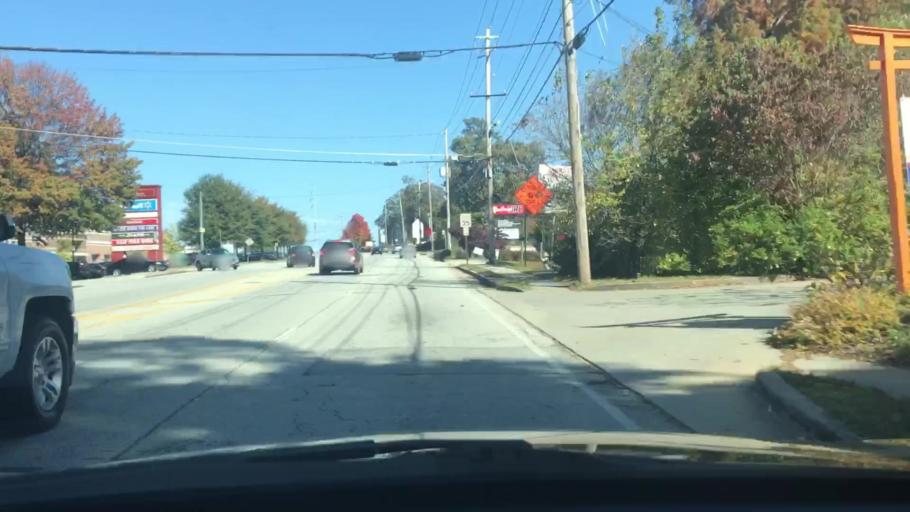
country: US
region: Georgia
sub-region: DeKalb County
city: Decatur
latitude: 33.7897
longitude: -84.2874
